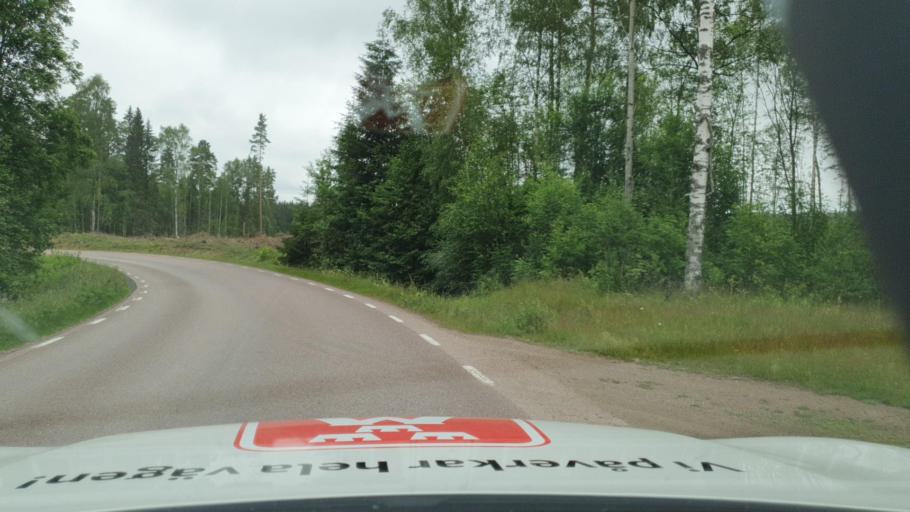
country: SE
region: Vaermland
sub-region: Kristinehamns Kommun
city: Kristinehamn
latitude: 59.4992
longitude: 13.9591
